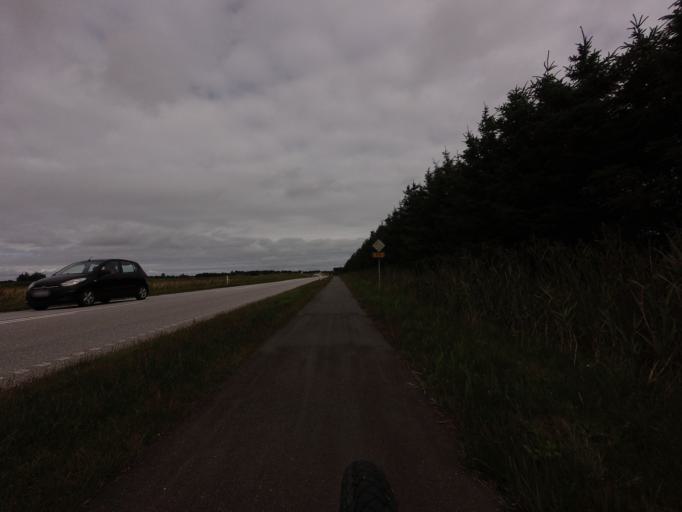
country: DK
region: North Denmark
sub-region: Hjorring Kommune
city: Hirtshals
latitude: 57.5565
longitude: 9.9391
